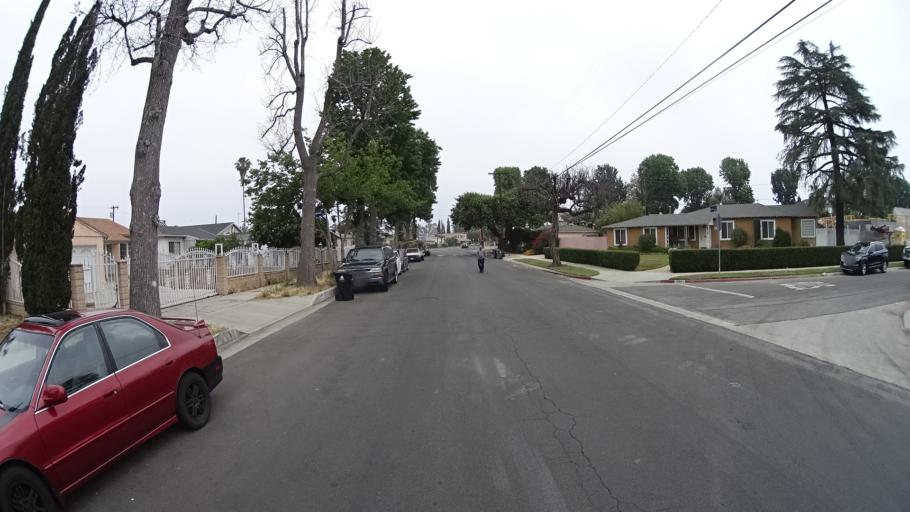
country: US
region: California
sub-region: Los Angeles County
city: Van Nuys
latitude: 34.1924
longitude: -118.4171
